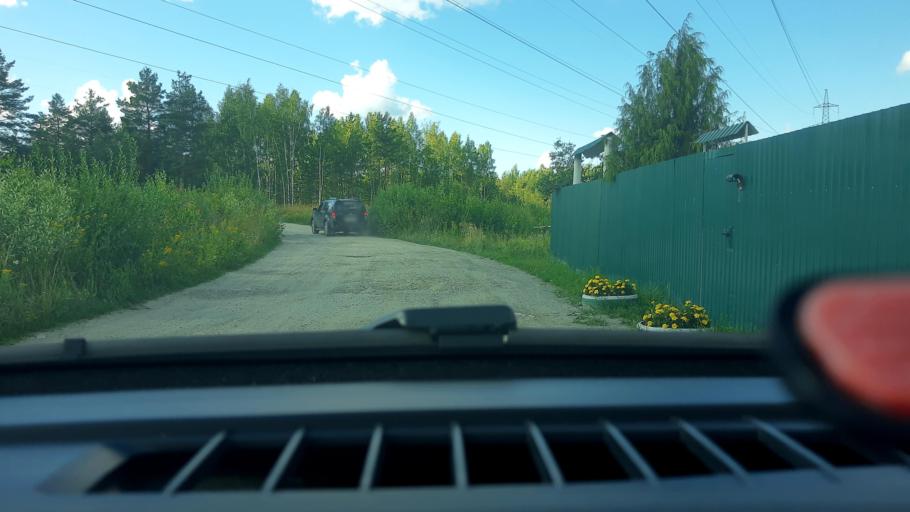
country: RU
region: Nizjnij Novgorod
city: Gorbatovka
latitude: 56.3349
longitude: 43.6666
